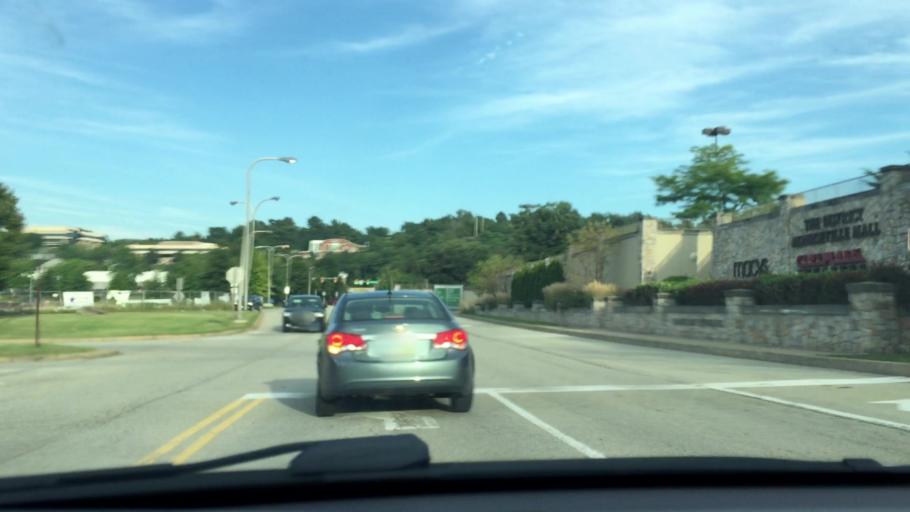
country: US
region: Pennsylvania
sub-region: Allegheny County
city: Monroeville
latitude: 40.4310
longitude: -79.7949
